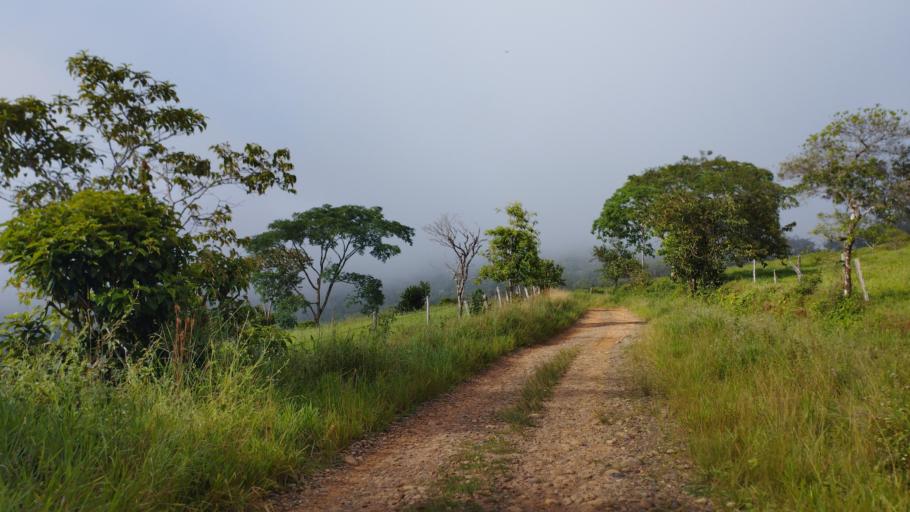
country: CO
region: Casanare
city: Sabanalarga
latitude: 4.7668
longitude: -73.0794
